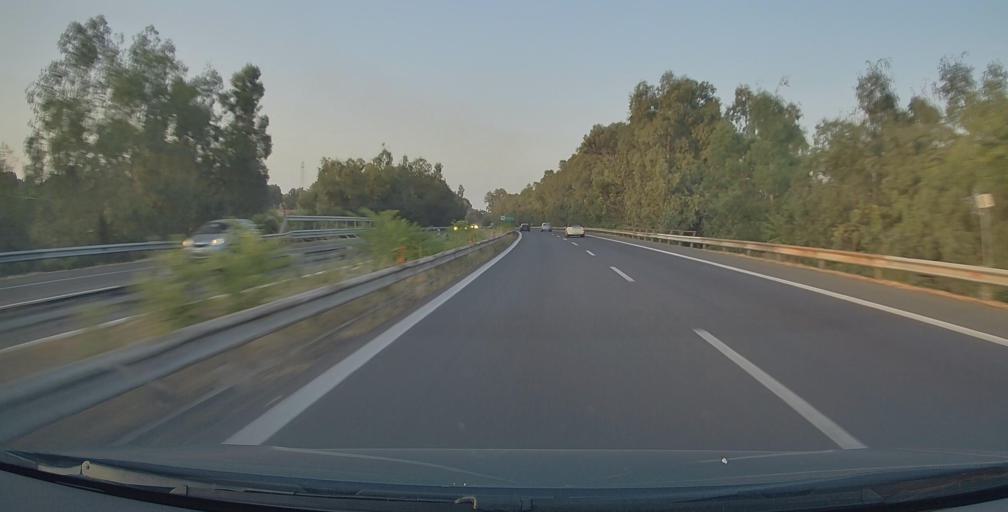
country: IT
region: Sicily
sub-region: Catania
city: Maugeri
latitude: 37.5809
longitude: 15.1198
